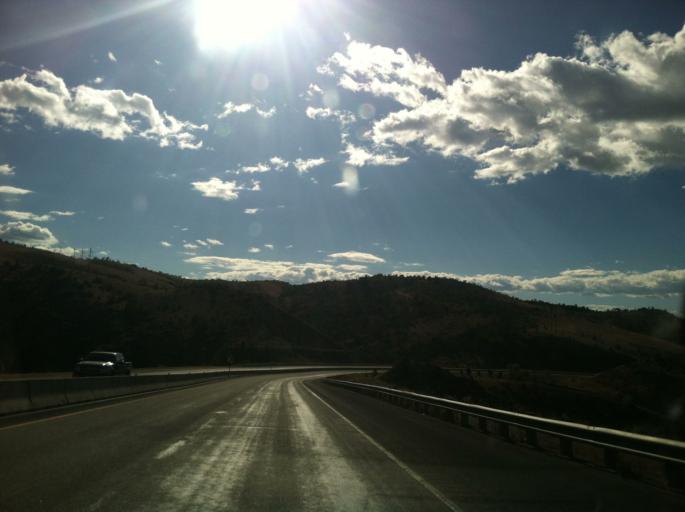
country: US
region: Montana
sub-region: Jefferson County
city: Whitehall
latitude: 45.8761
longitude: -111.8881
